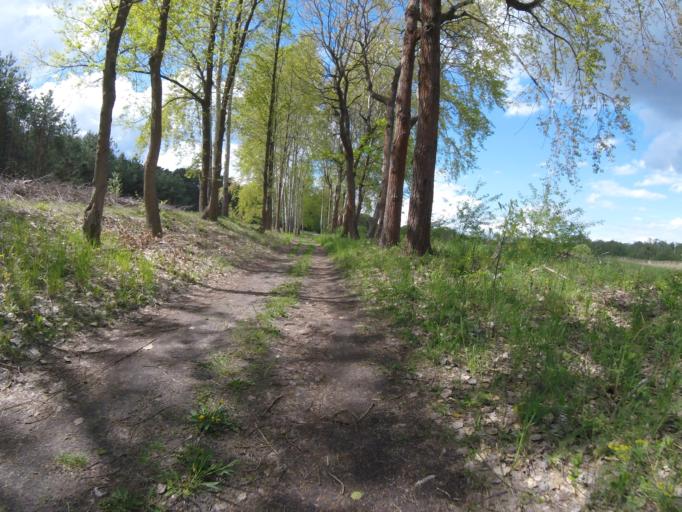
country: DE
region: Brandenburg
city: Teupitz
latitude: 52.1194
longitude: 13.6020
